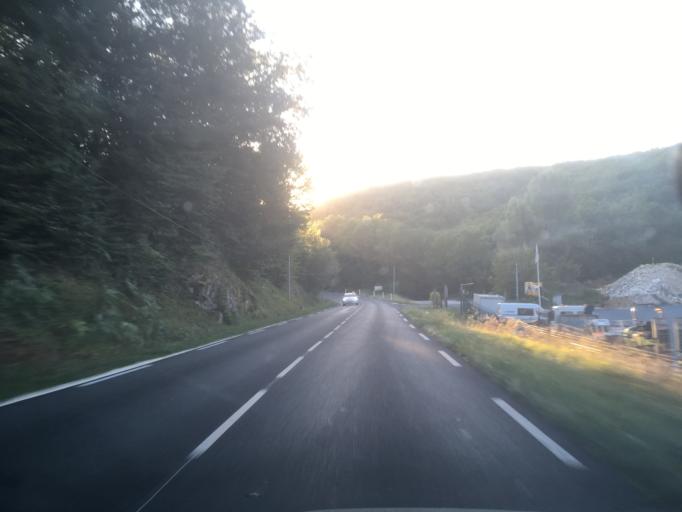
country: FR
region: Aquitaine
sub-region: Departement de la Dordogne
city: Sarlat-la-Caneda
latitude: 44.8524
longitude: 1.1974
